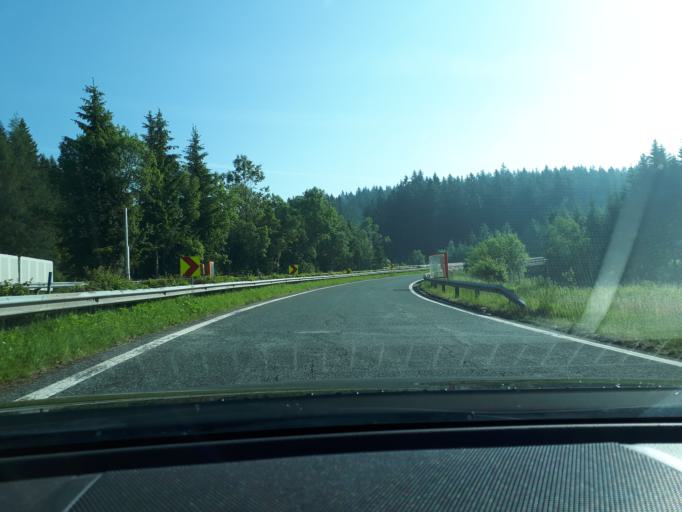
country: AT
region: Styria
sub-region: Politischer Bezirk Voitsberg
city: Pack
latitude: 46.9634
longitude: 14.9585
